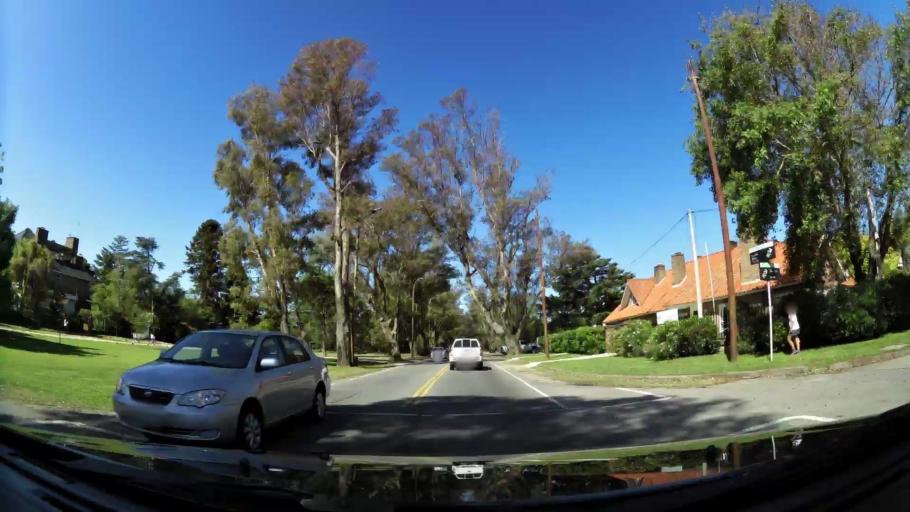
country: UY
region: Canelones
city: Barra de Carrasco
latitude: -34.8836
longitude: -56.0510
